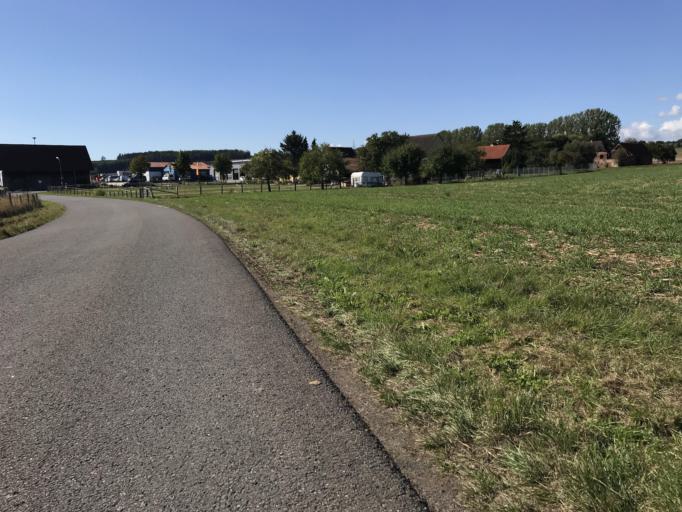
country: DE
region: Hesse
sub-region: Regierungsbezirk Kassel
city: Vohl
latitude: 51.2577
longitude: 8.9336
